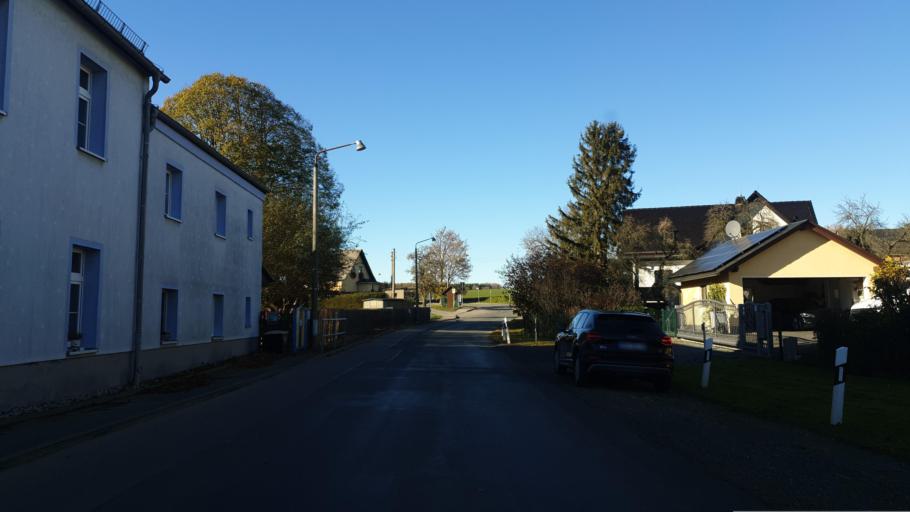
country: DE
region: Saxony
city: Elsterberg
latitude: 50.6404
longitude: 12.1504
